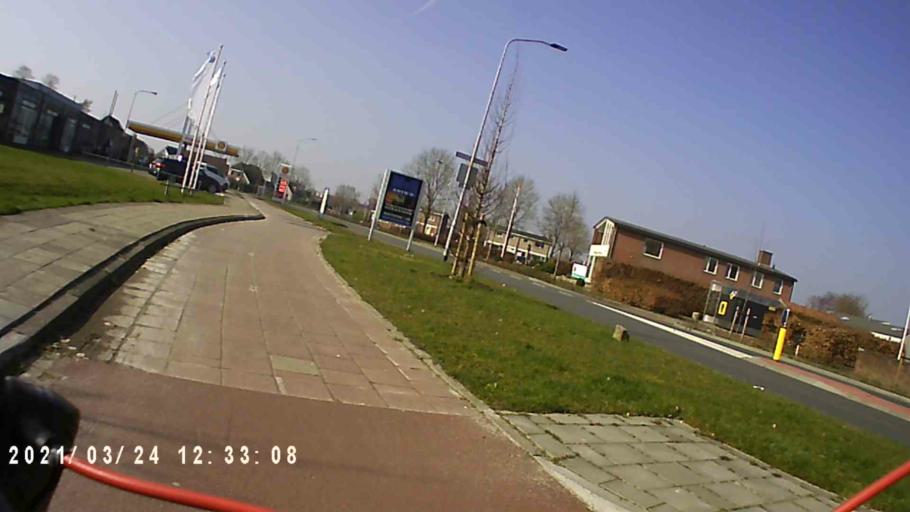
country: NL
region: Groningen
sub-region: Gemeente Leek
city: Leek
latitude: 53.1710
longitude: 6.3642
